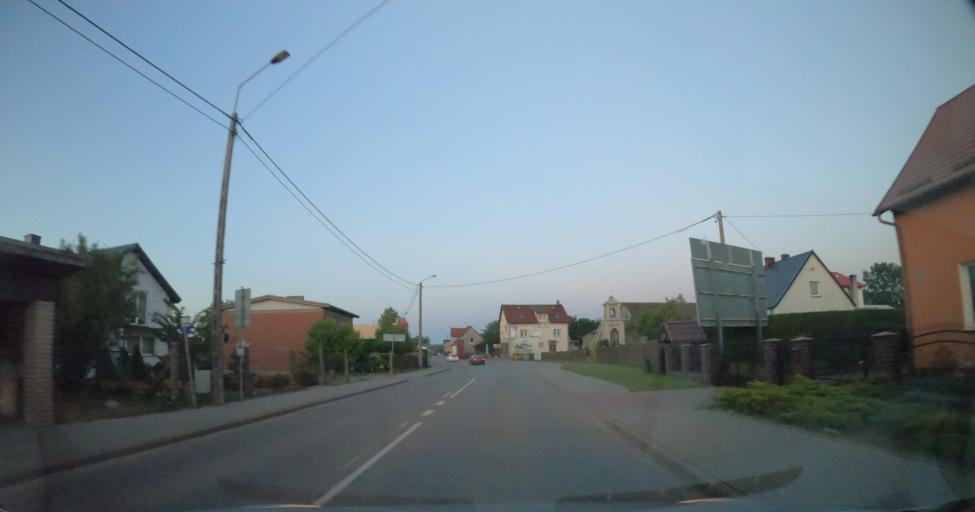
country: PL
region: Pomeranian Voivodeship
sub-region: Powiat wejherowski
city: Szemud
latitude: 54.4867
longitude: 18.2209
